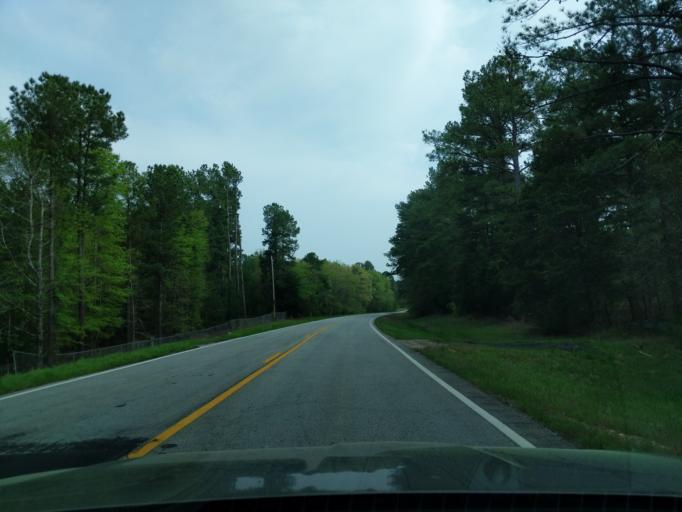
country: US
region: Georgia
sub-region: Lincoln County
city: Lincolnton
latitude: 33.8120
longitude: -82.4088
